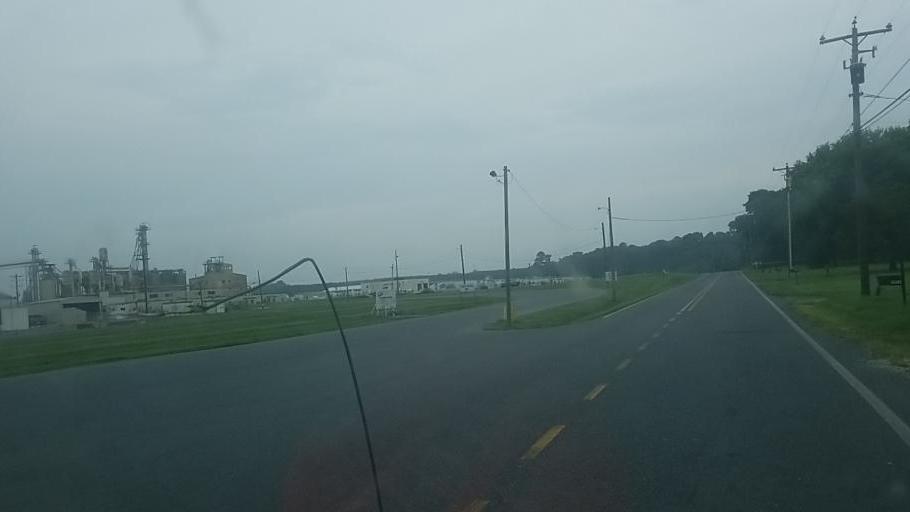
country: US
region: Maryland
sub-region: Wicomico County
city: Salisbury
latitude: 38.3818
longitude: -75.5258
